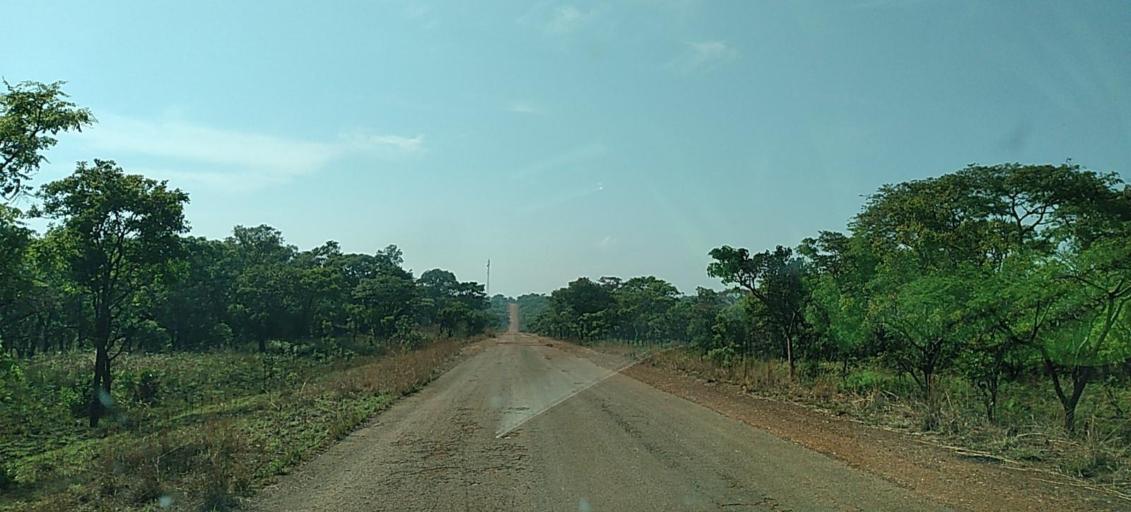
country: ZM
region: North-Western
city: Mwinilunga
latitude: -11.8030
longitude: 25.0775
